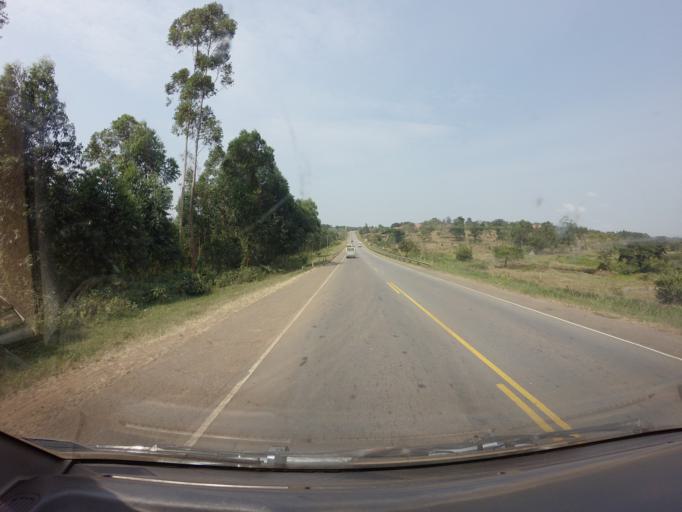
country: UG
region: Central Region
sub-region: Lwengo District
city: Lwengo
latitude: -0.3960
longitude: 31.4134
